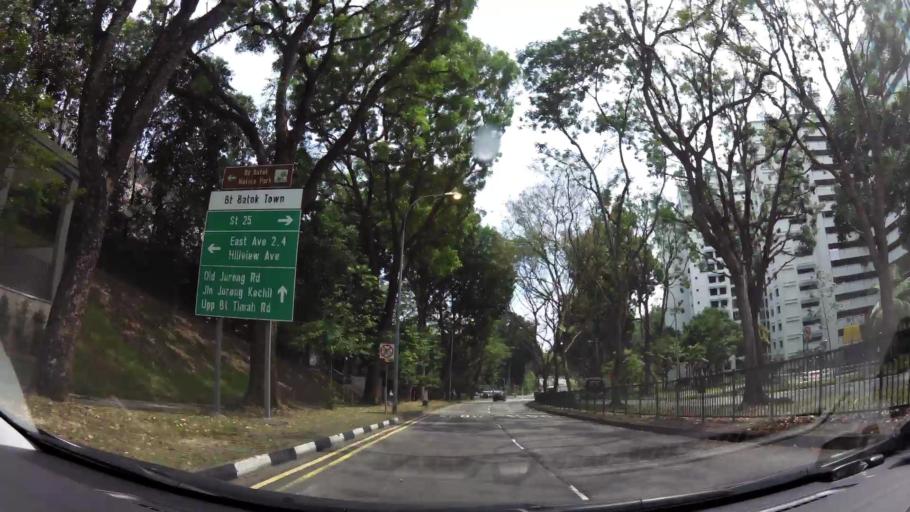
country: SG
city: Singapore
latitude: 1.3467
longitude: 103.7596
